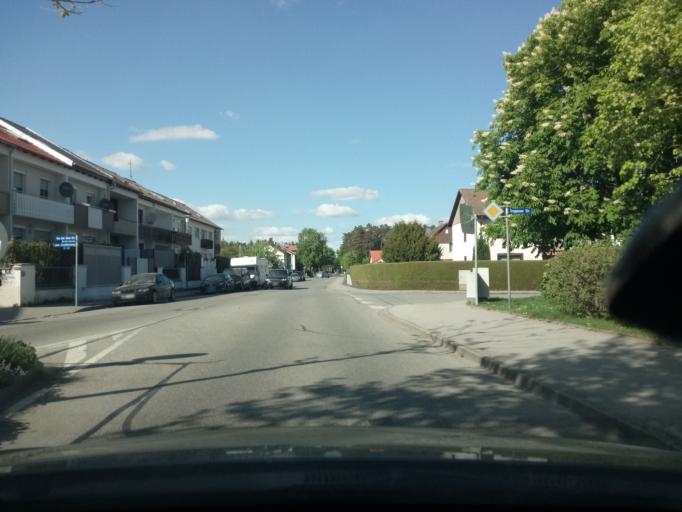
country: DE
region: Bavaria
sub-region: Upper Bavaria
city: Waldkraiburg
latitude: 48.2021
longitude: 12.3839
